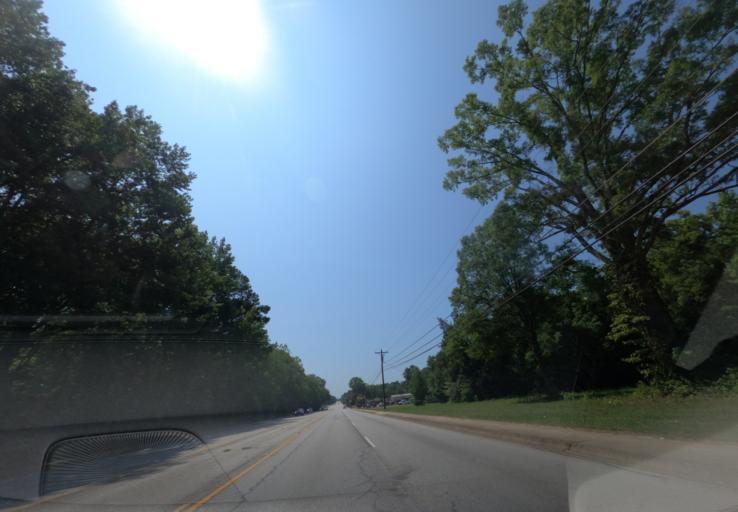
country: US
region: South Carolina
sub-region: Greenwood County
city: Greenwood
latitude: 34.1509
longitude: -82.1378
